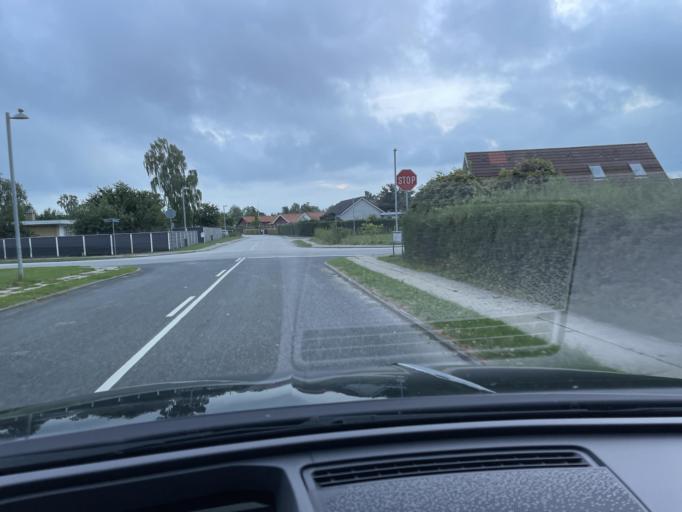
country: DK
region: Zealand
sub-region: Solrod Kommune
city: Havdrup
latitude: 55.5480
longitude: 12.1265
